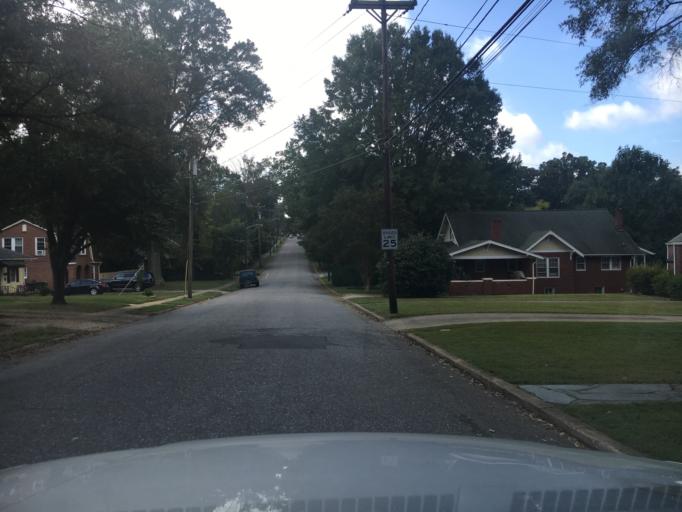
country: US
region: North Carolina
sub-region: Catawba County
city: Hickory
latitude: 35.7429
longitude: -81.3376
